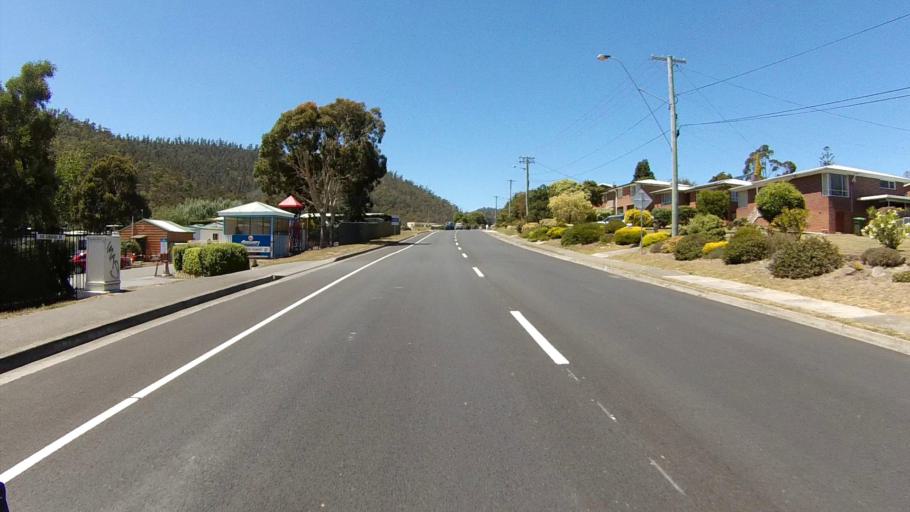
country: AU
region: Tasmania
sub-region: Clarence
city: Warrane
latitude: -42.8559
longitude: 147.3968
